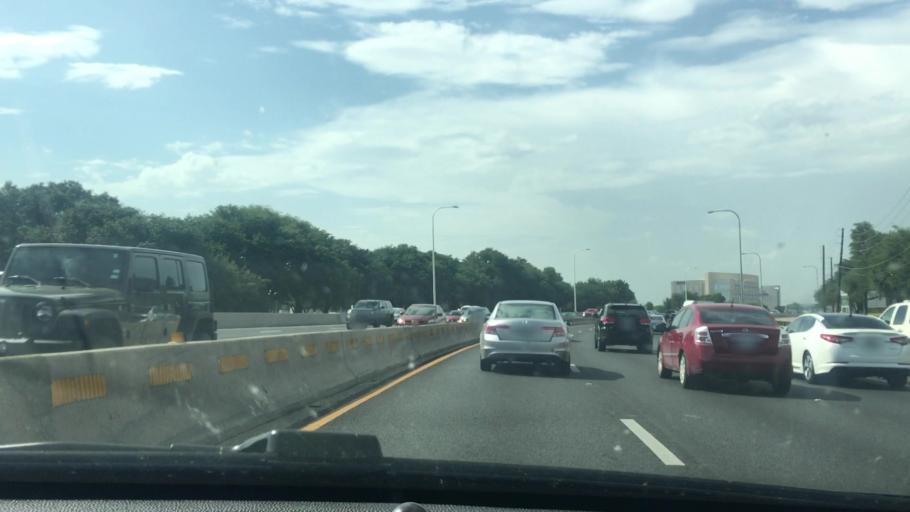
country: US
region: Texas
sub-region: Dallas County
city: Addison
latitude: 32.9796
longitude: -96.8283
